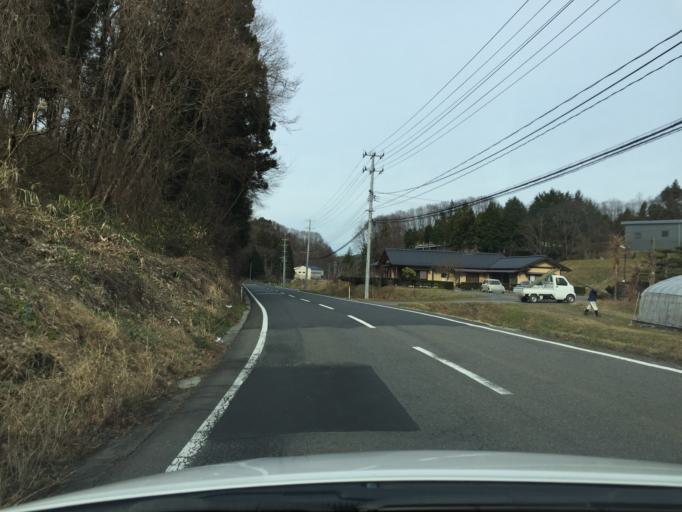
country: JP
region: Fukushima
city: Ishikawa
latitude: 37.2316
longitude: 140.6300
